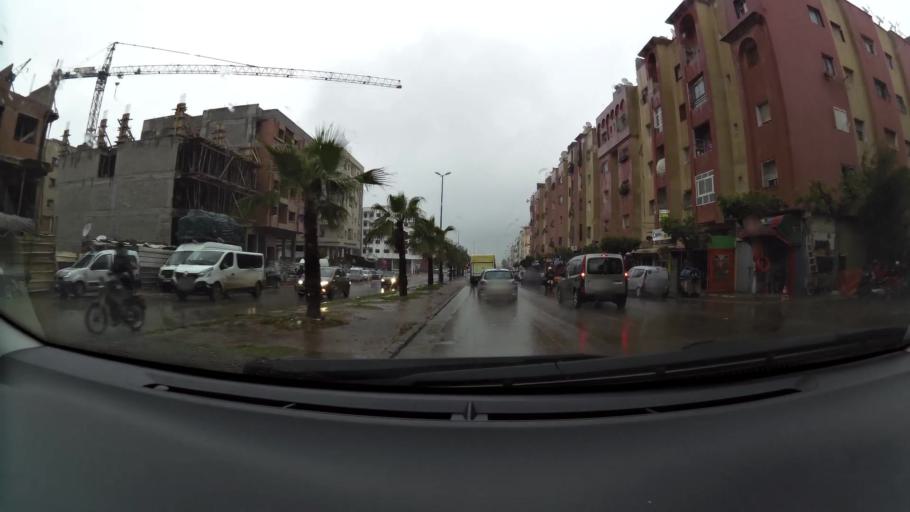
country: MA
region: Grand Casablanca
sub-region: Mediouna
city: Tit Mellil
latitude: 33.5917
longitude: -7.4987
